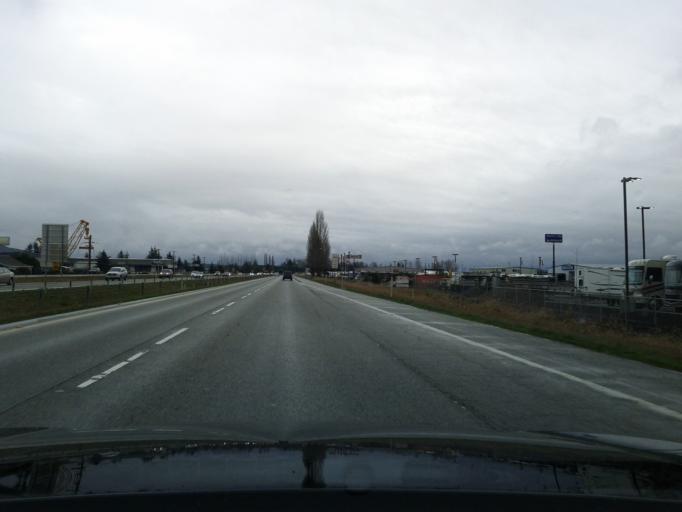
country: US
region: Washington
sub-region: Skagit County
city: Mount Vernon
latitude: 48.3939
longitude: -122.3307
